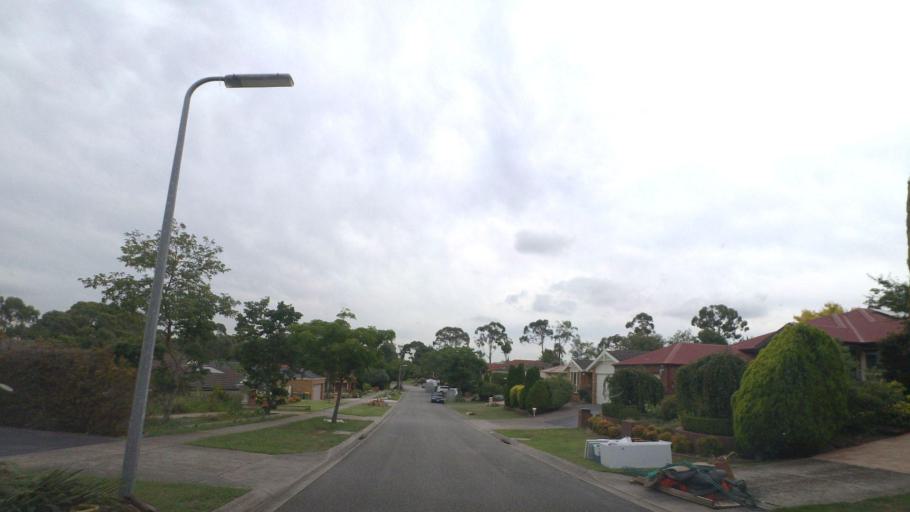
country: AU
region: Victoria
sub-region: Yarra Ranges
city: Lilydale
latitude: -37.7754
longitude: 145.3421
